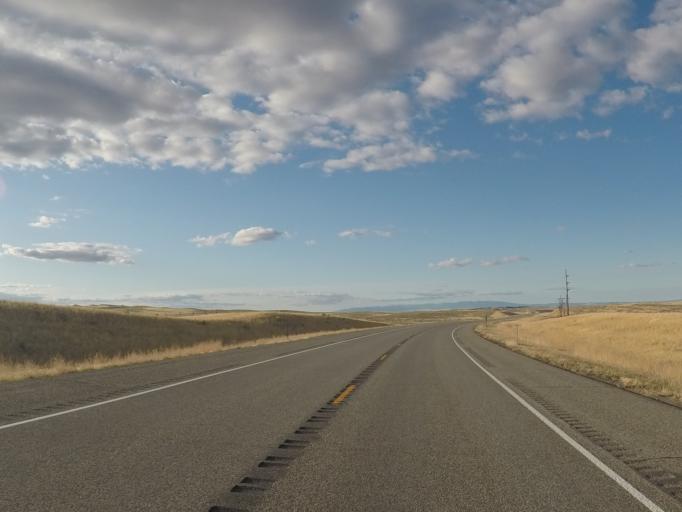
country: US
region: Montana
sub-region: Golden Valley County
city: Ryegate
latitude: 46.1700
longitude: -108.9052
